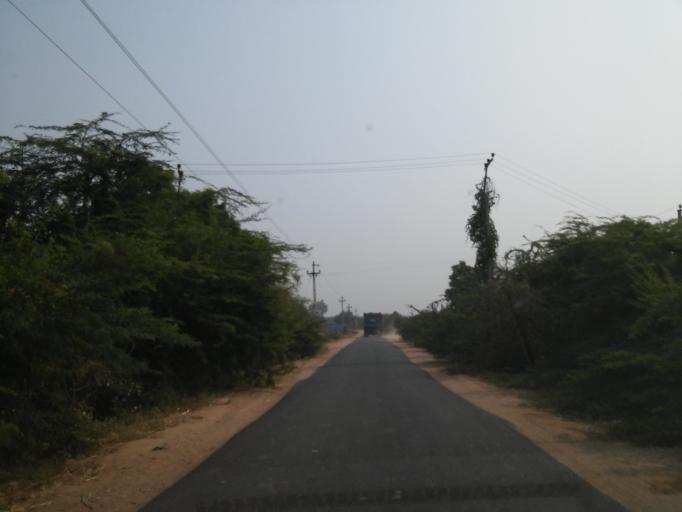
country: IN
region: Gujarat
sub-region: Kachchh
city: Bhuj
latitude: 23.4307
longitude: 69.6896
